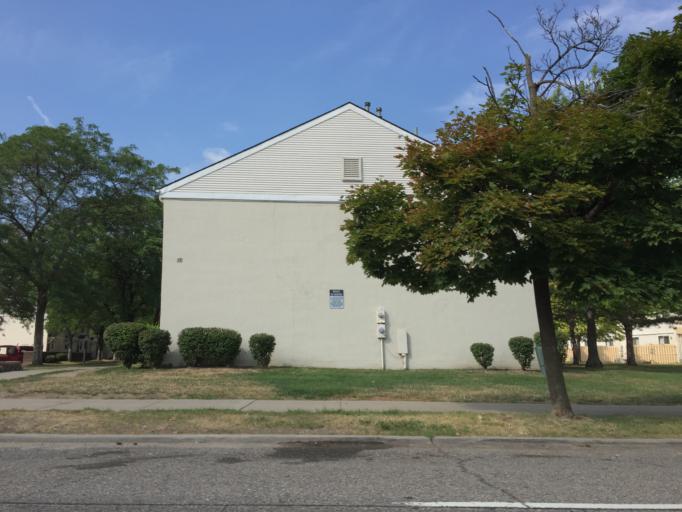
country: US
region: Michigan
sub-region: Wayne County
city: Detroit
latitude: 42.3404
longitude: -83.0243
